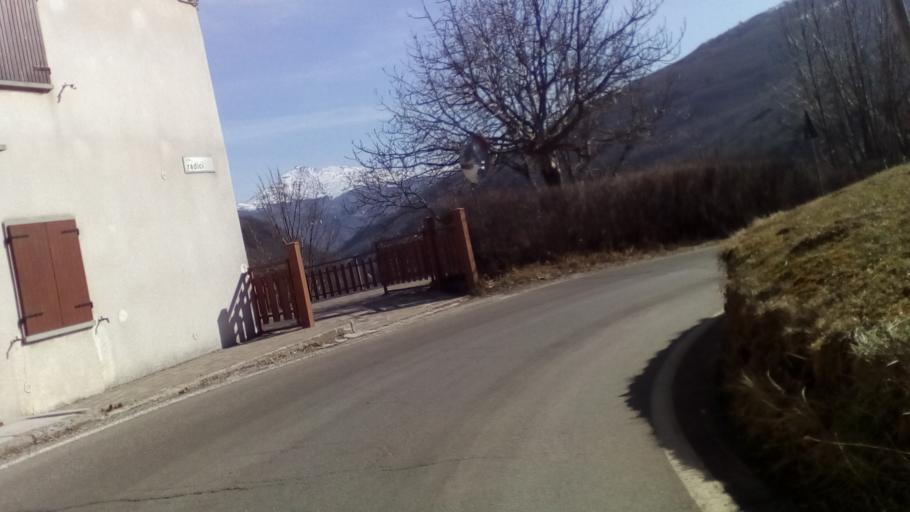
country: IT
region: Emilia-Romagna
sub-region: Provincia di Modena
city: Pievepelago
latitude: 44.1909
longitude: 10.5562
